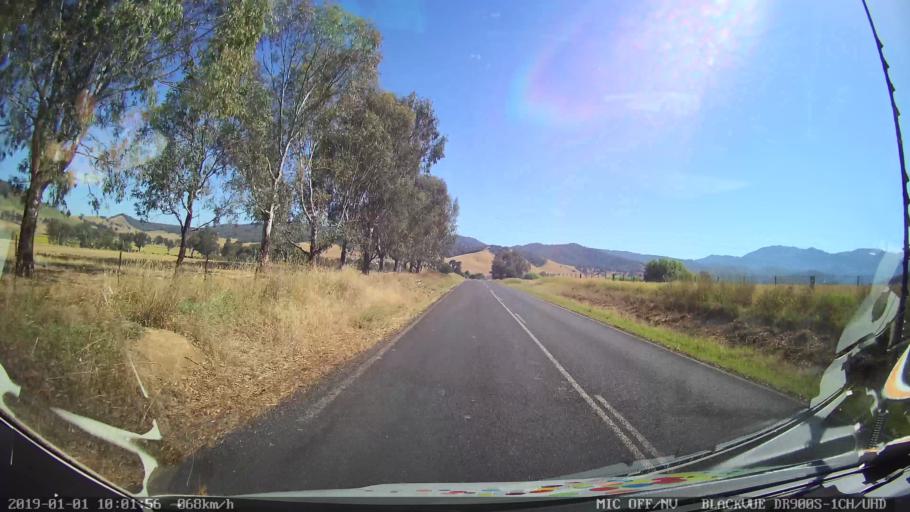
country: AU
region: New South Wales
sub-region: Snowy River
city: Jindabyne
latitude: -36.1864
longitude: 148.1011
